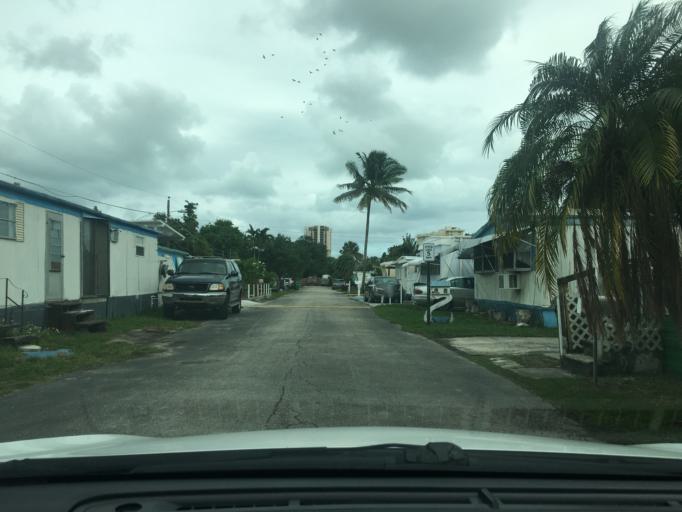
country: US
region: Florida
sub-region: Miami-Dade County
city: Biscayne Park
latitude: 25.8806
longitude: -80.1693
